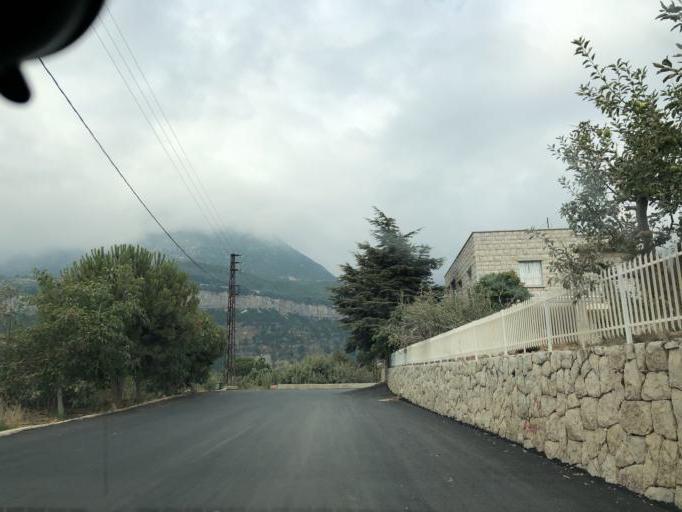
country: LB
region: Liban-Nord
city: Bcharre
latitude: 34.0811
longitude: 35.8724
